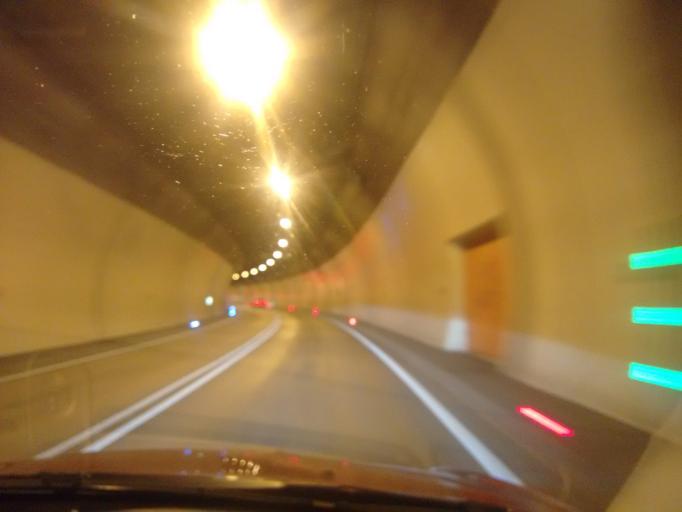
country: AT
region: Upper Austria
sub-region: Politischer Bezirk Gmunden
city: Ebensee
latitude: 47.8400
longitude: 13.7837
